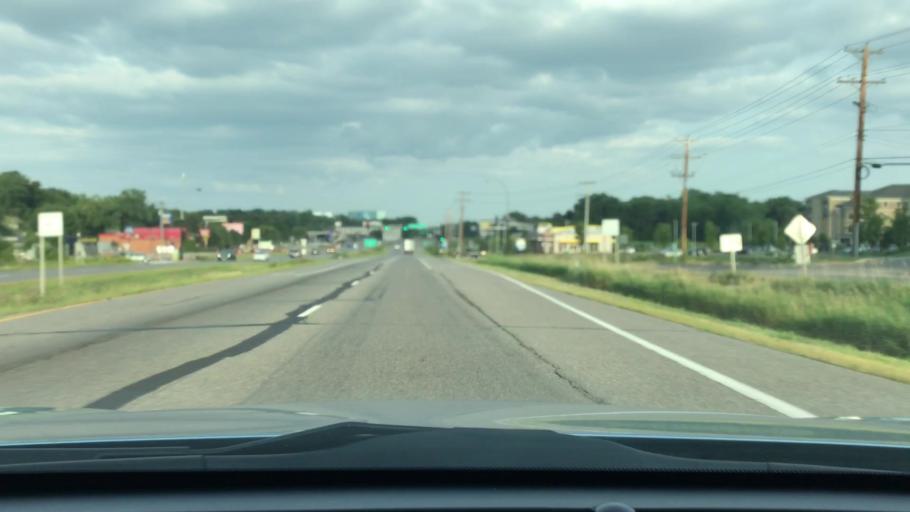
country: US
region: Minnesota
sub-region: Hennepin County
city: Plymouth
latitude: 44.9892
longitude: -93.4258
